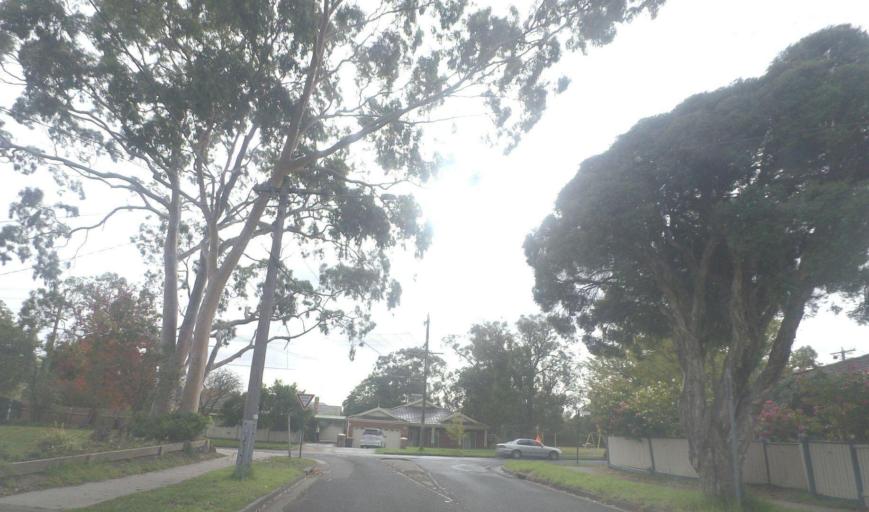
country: AU
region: Victoria
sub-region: Whitehorse
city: Nunawading
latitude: -37.8105
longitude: 145.1716
